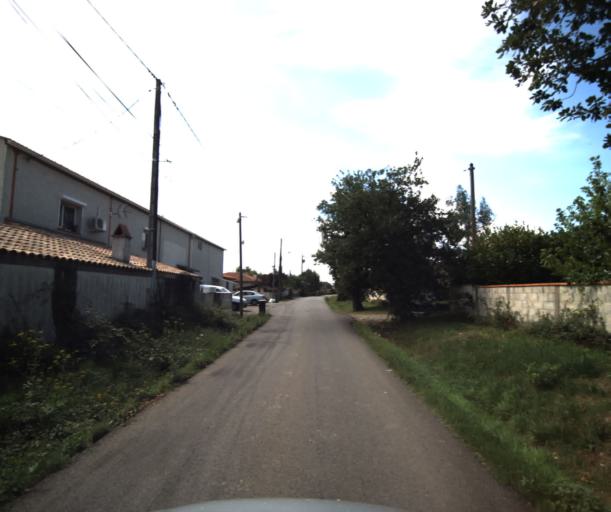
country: FR
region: Midi-Pyrenees
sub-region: Departement de la Haute-Garonne
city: Lacasse
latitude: 43.3915
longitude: 1.2638
